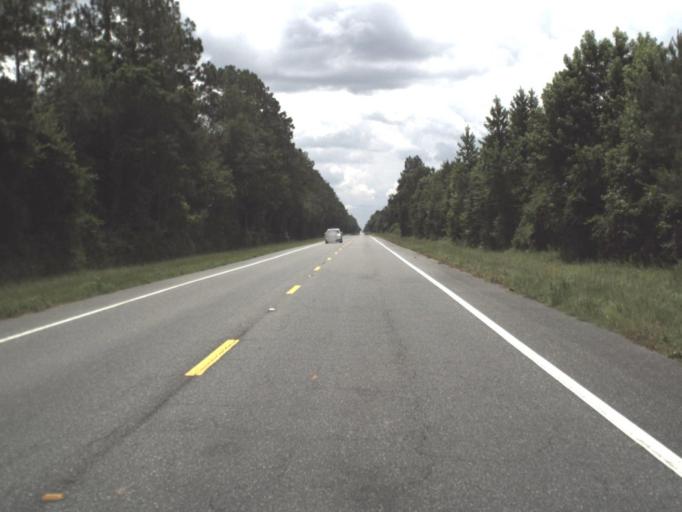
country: US
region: Florida
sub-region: Columbia County
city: Watertown
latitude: 30.1409
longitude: -82.5386
